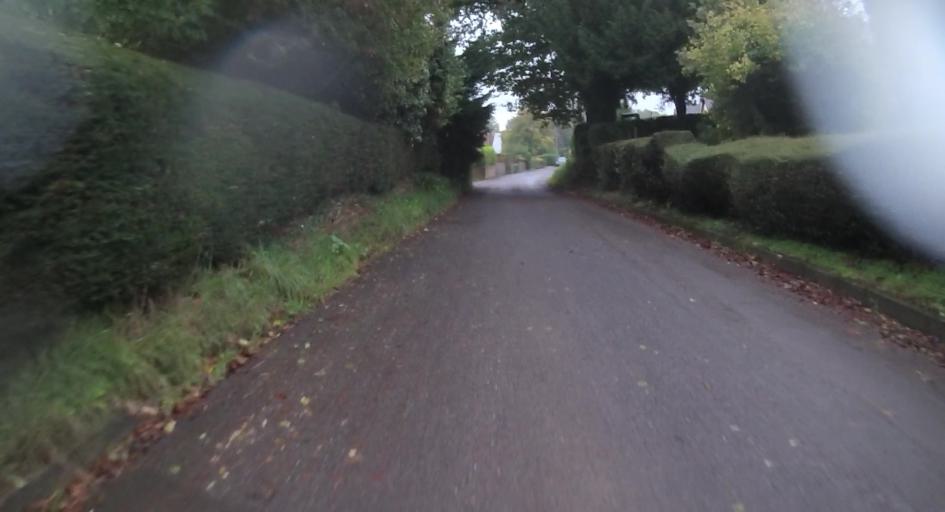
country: GB
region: England
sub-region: West Berkshire
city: Thatcham
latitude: 51.4033
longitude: -1.2059
